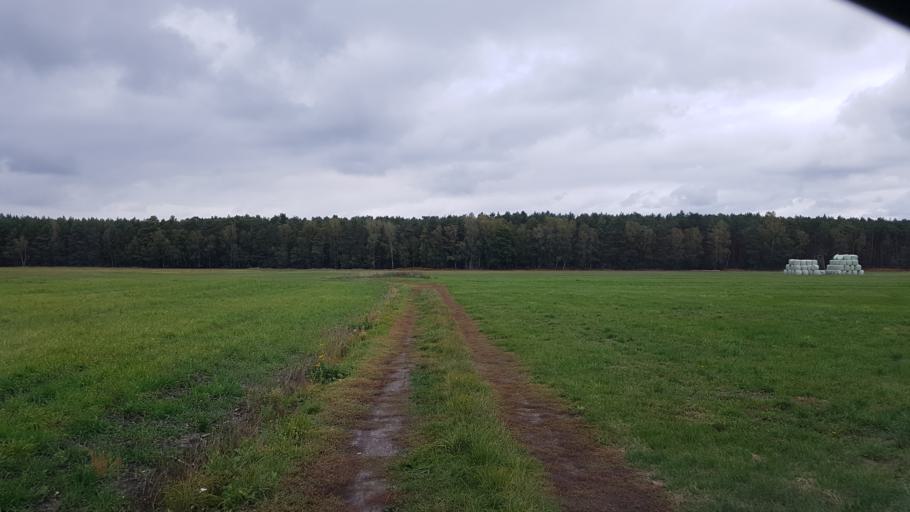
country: DE
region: Brandenburg
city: Finsterwalde
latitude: 51.5784
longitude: 13.6726
